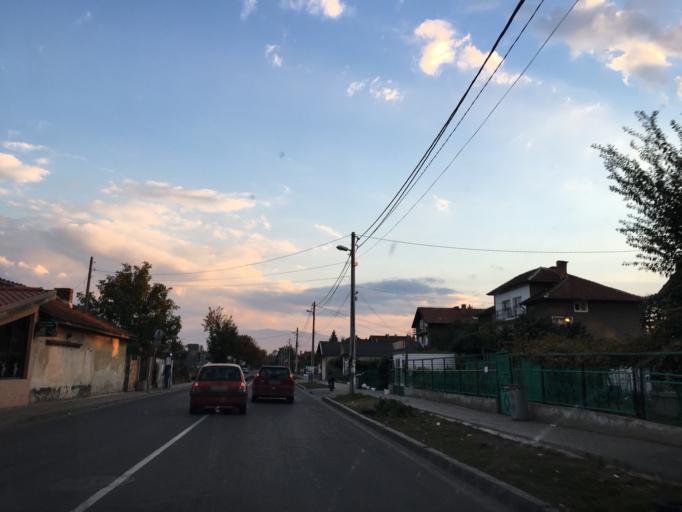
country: BG
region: Sofia-Capital
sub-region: Stolichna Obshtina
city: Sofia
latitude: 42.8003
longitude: 23.3410
